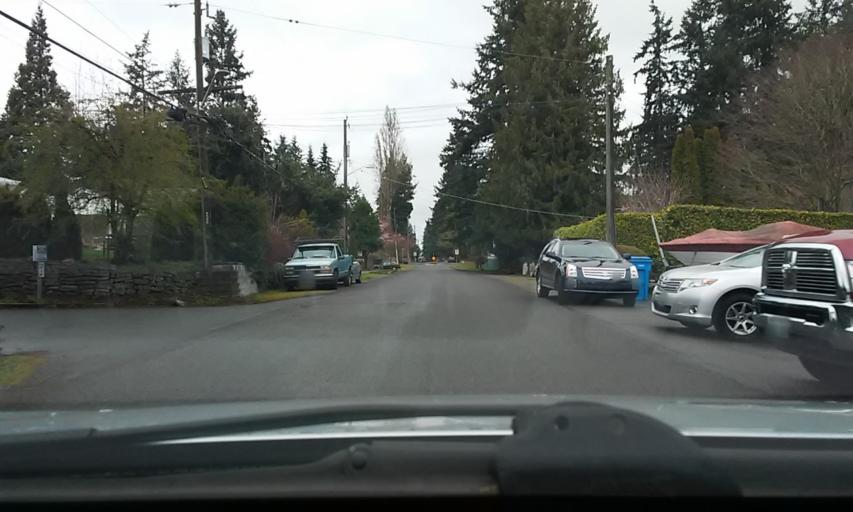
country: US
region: Washington
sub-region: King County
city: Shoreline
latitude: 47.7602
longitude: -122.3377
